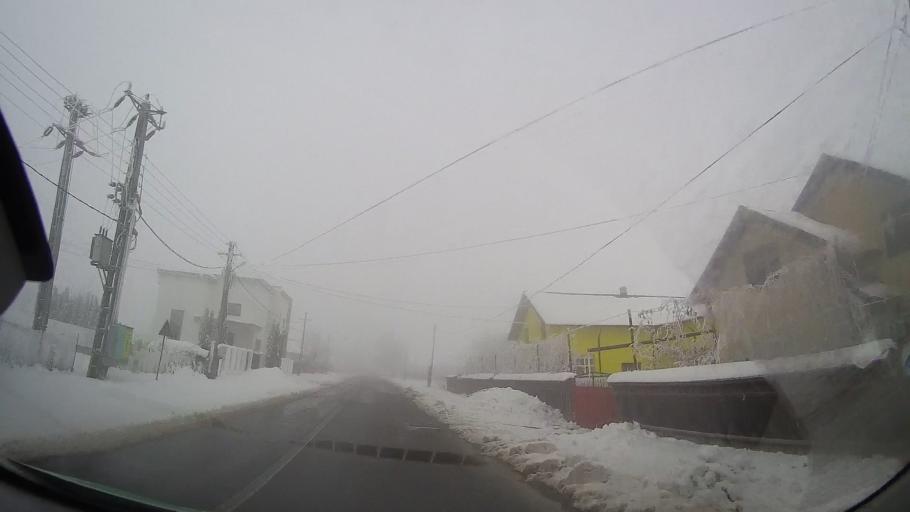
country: RO
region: Neamt
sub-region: Comuna Sabaoani
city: Sabaoani
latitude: 47.0245
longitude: 26.8625
